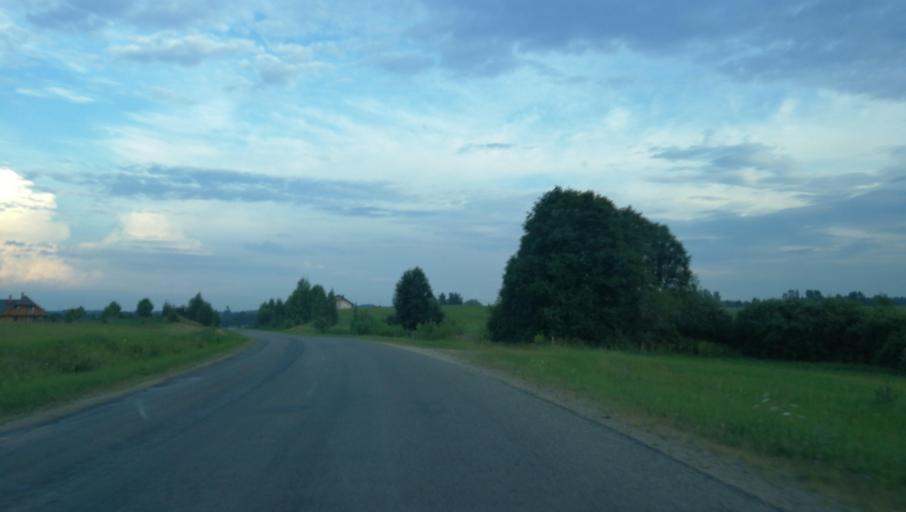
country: LV
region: Cesu Rajons
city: Cesis
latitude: 57.2835
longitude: 25.3133
